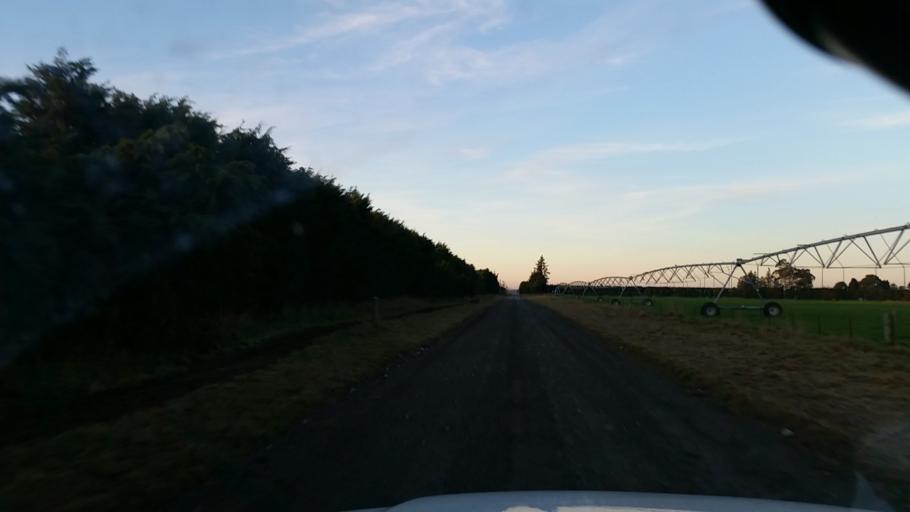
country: NZ
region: Canterbury
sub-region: Ashburton District
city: Methven
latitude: -43.7897
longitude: 171.5246
